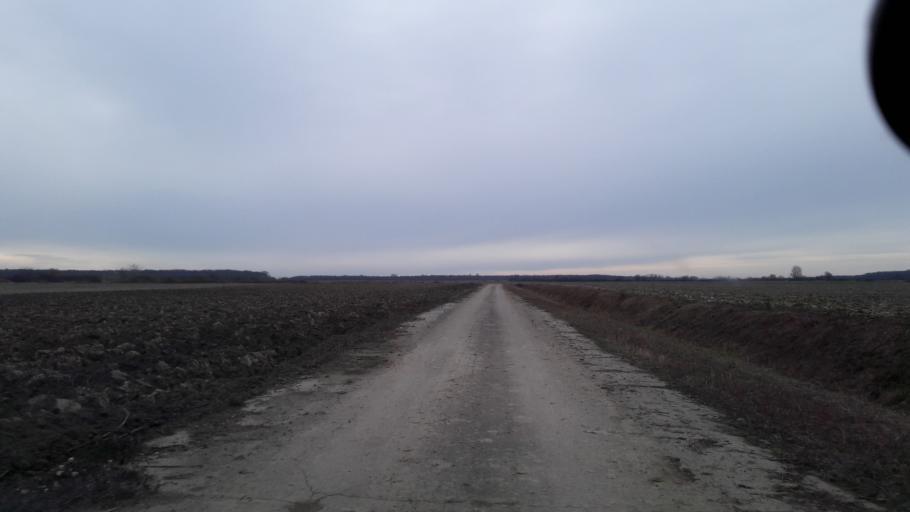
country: HR
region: Osjecko-Baranjska
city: Vladislavci
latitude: 45.4286
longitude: 18.5739
